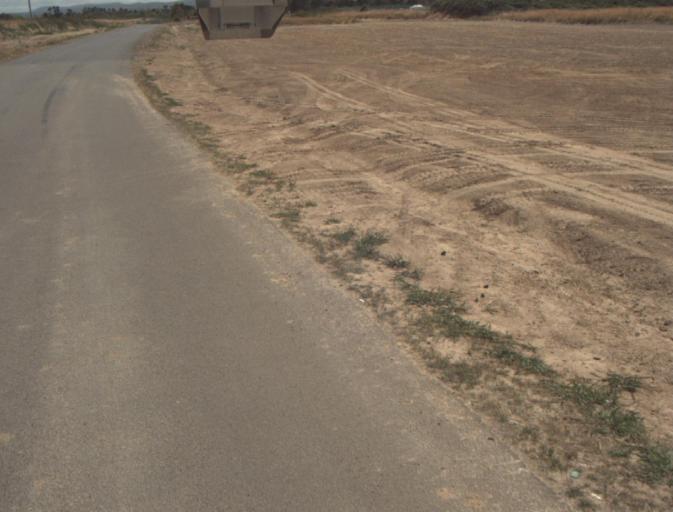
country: AU
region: Tasmania
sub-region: Launceston
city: Launceston
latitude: -41.4234
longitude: 147.1225
